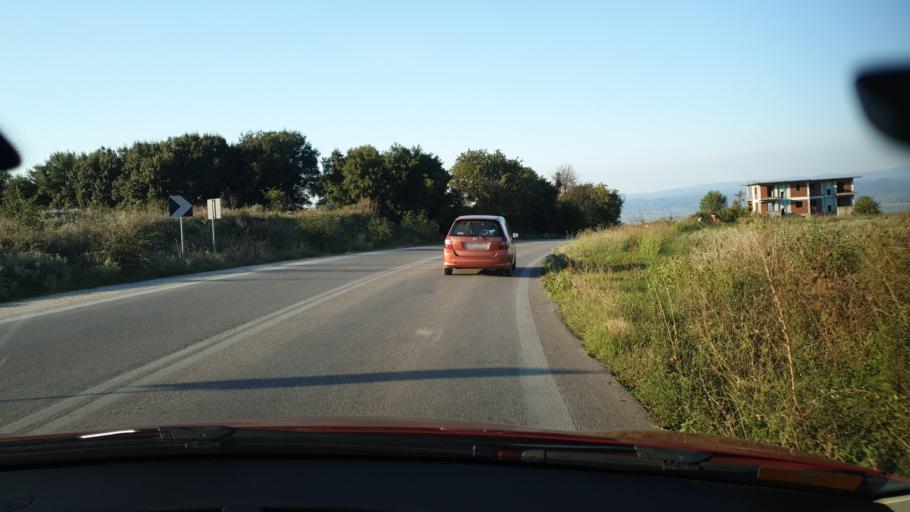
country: GR
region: Central Macedonia
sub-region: Nomos Thessalonikis
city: Agios Vasileios
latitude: 40.6501
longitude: 23.1131
